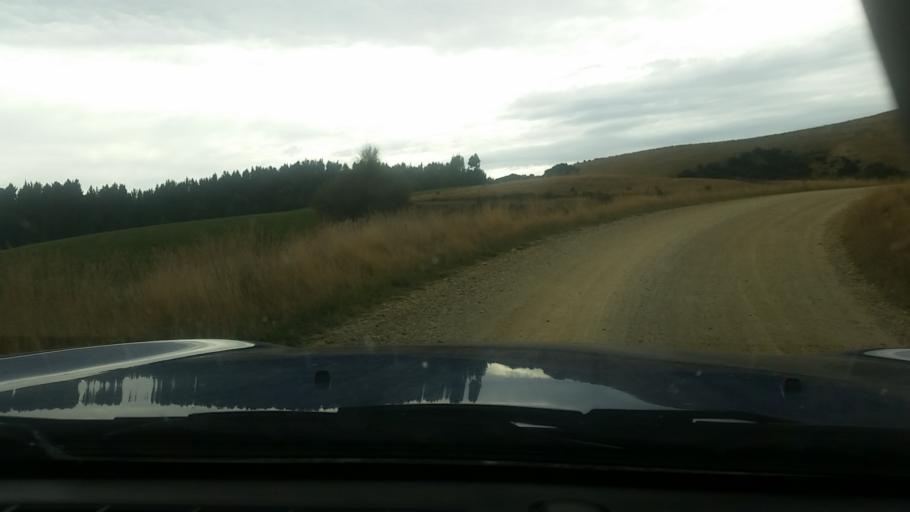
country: NZ
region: Otago
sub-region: Clutha District
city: Balclutha
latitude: -45.7029
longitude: 169.4754
